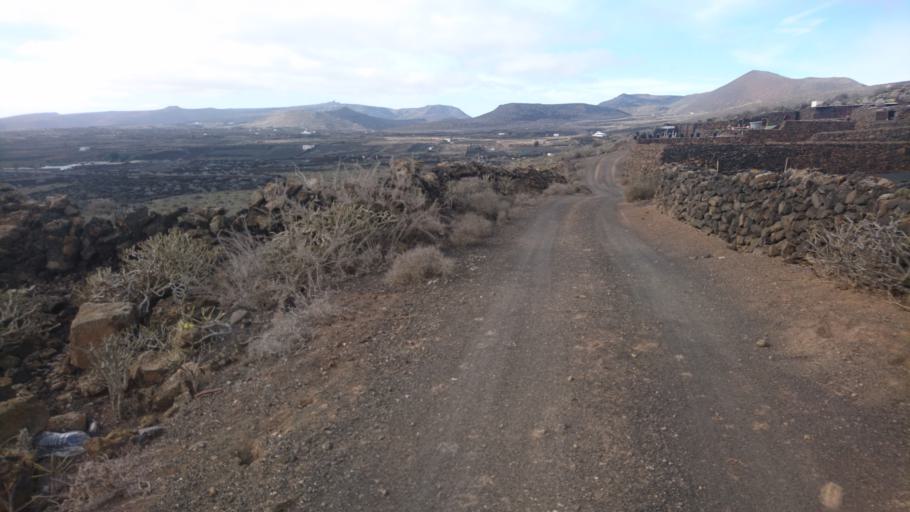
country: ES
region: Canary Islands
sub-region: Provincia de Las Palmas
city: Haria
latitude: 29.1762
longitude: -13.4655
